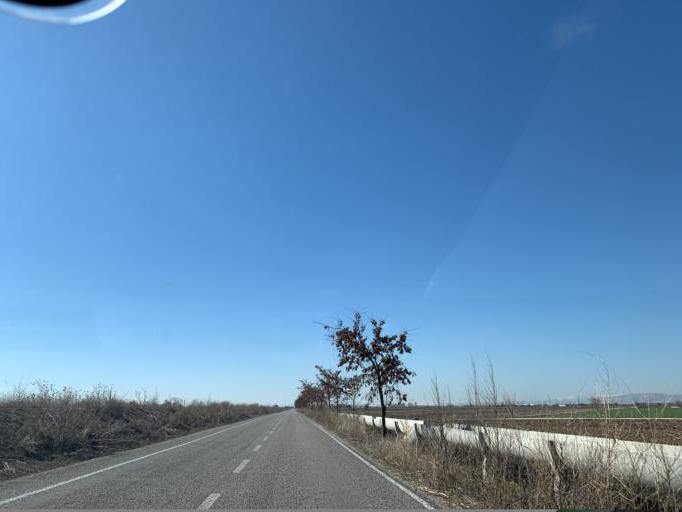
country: TR
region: Konya
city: Catalhoeyuek
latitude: 37.6247
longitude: 32.8049
